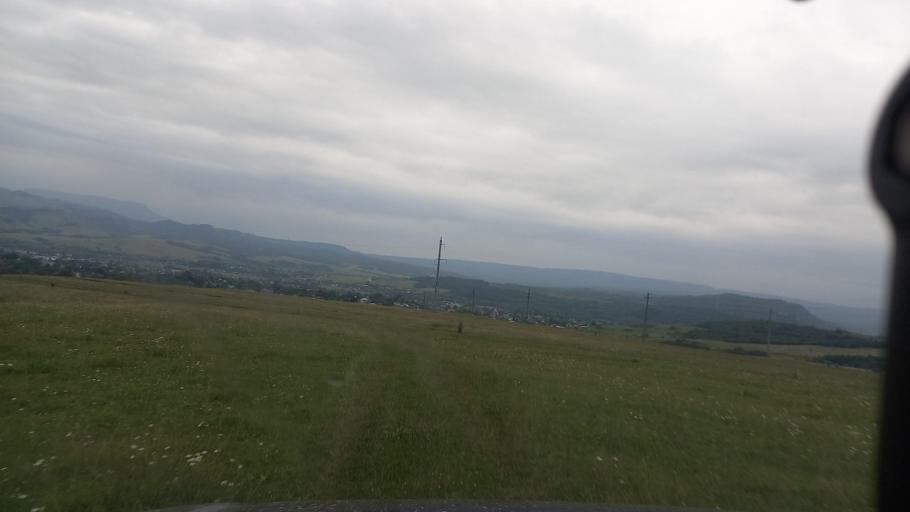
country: RU
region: Karachayevo-Cherkesiya
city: Pregradnaya
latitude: 43.9489
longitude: 41.1632
